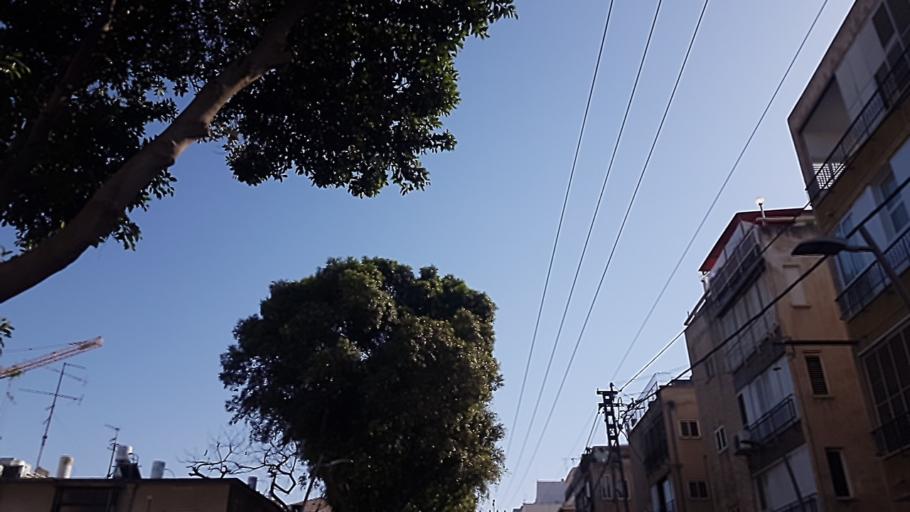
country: IL
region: Tel Aviv
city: Bene Beraq
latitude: 32.0778
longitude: 34.8232
